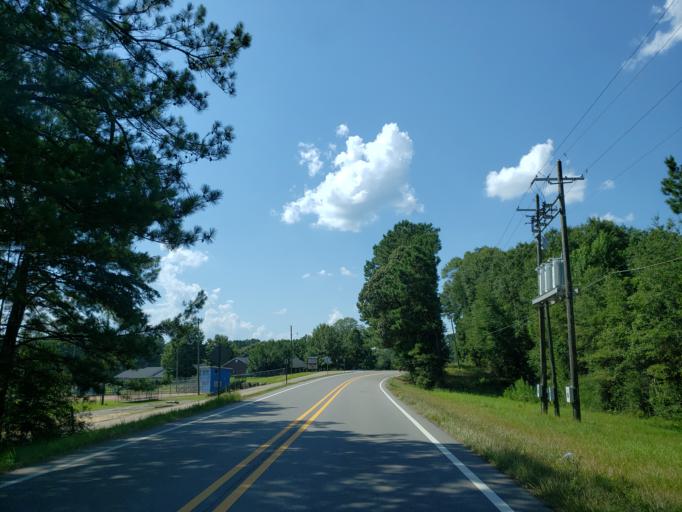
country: US
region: Mississippi
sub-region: Lamar County
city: Sumrall
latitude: 31.4068
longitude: -89.5449
